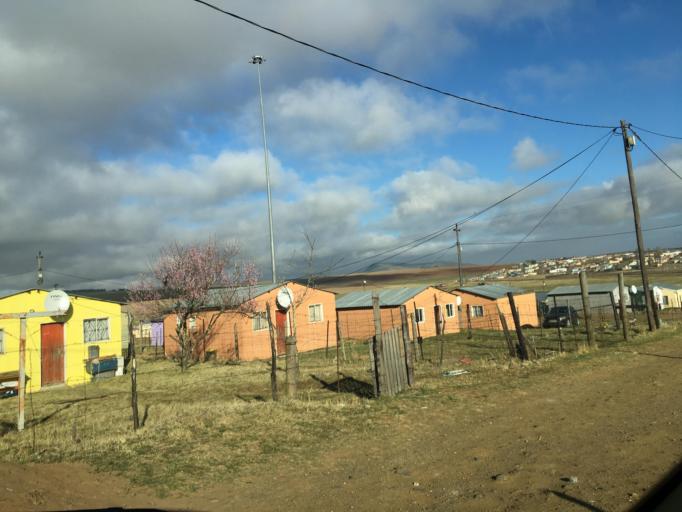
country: ZA
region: Eastern Cape
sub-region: Chris Hani District Municipality
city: Elliot
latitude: -31.3353
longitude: 27.8334
